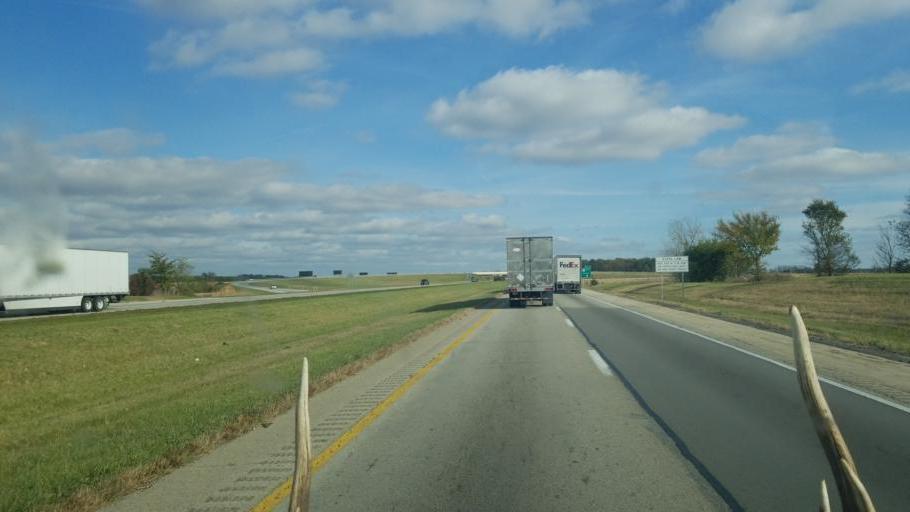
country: US
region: Ohio
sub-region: Preble County
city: New Paris
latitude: 39.8285
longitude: -84.7888
